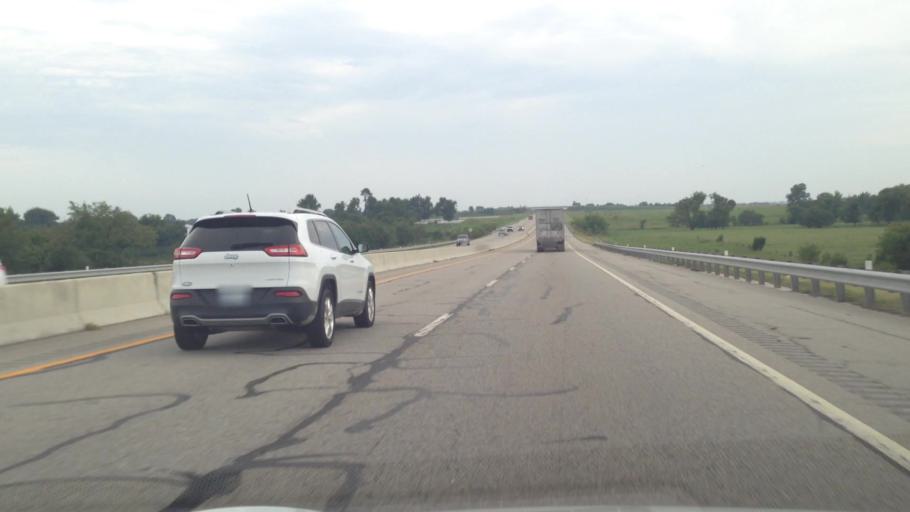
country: US
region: Oklahoma
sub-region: Ottawa County
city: Miami
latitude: 36.8121
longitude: -94.8752
